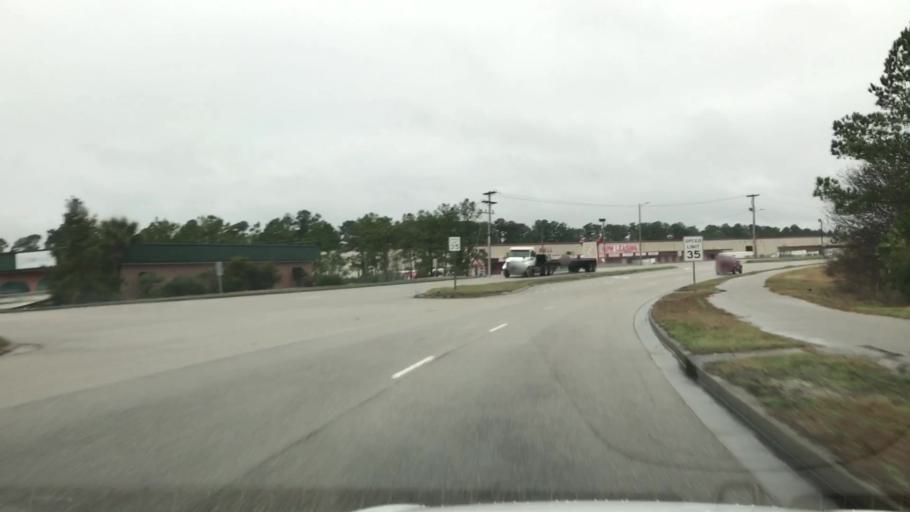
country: US
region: South Carolina
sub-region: Horry County
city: Forestbrook
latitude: 33.7094
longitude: -78.9402
